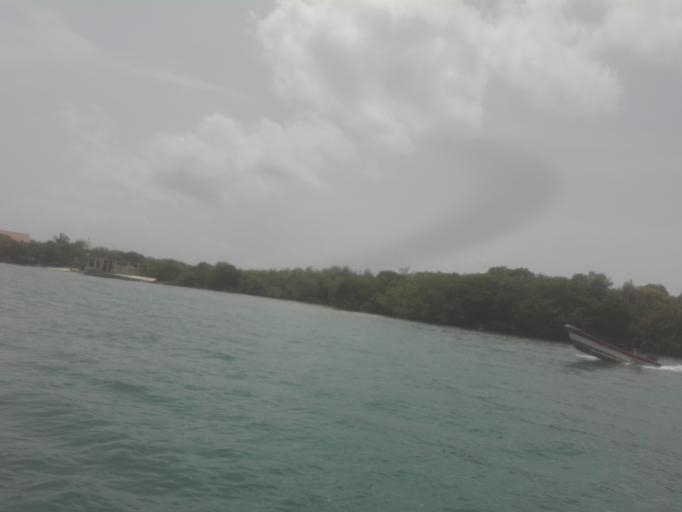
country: CO
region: Bolivar
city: Turbana
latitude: 10.1650
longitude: -75.6700
